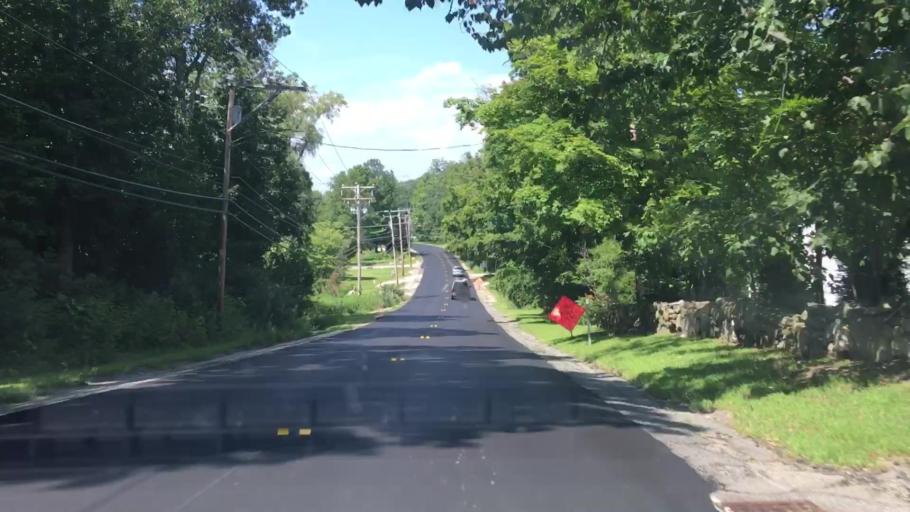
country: US
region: New Hampshire
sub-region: Rockingham County
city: Hampstead
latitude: 42.8830
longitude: -71.1886
